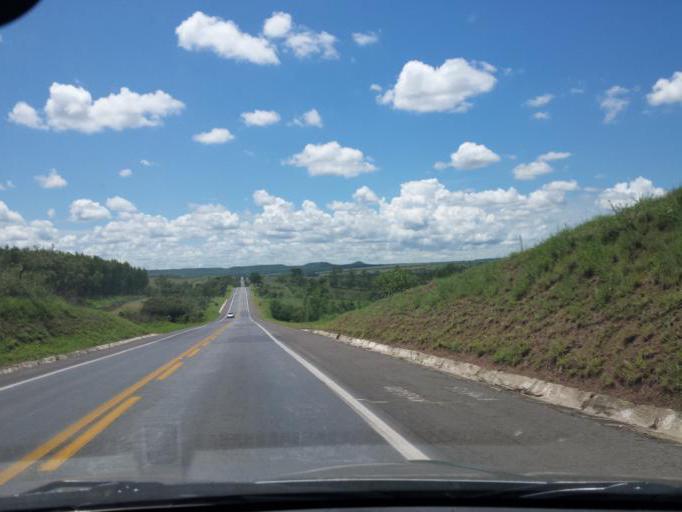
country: BR
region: Goias
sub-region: Cristalina
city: Cristalina
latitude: -16.5773
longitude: -47.7859
